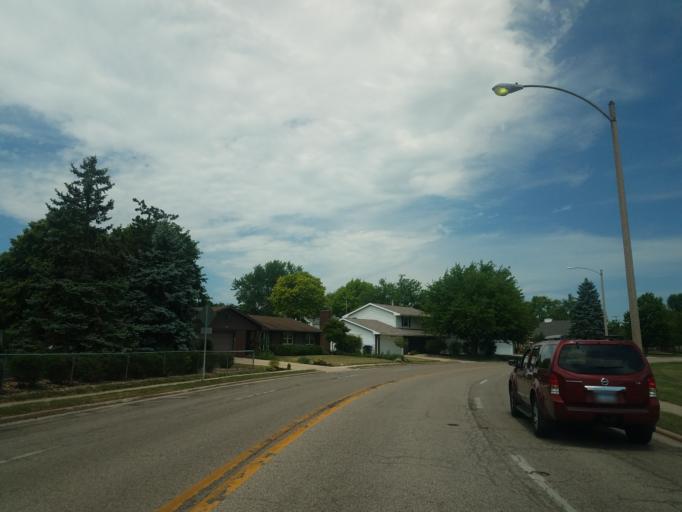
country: US
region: Illinois
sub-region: McLean County
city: Bloomington
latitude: 40.4785
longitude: -88.9590
